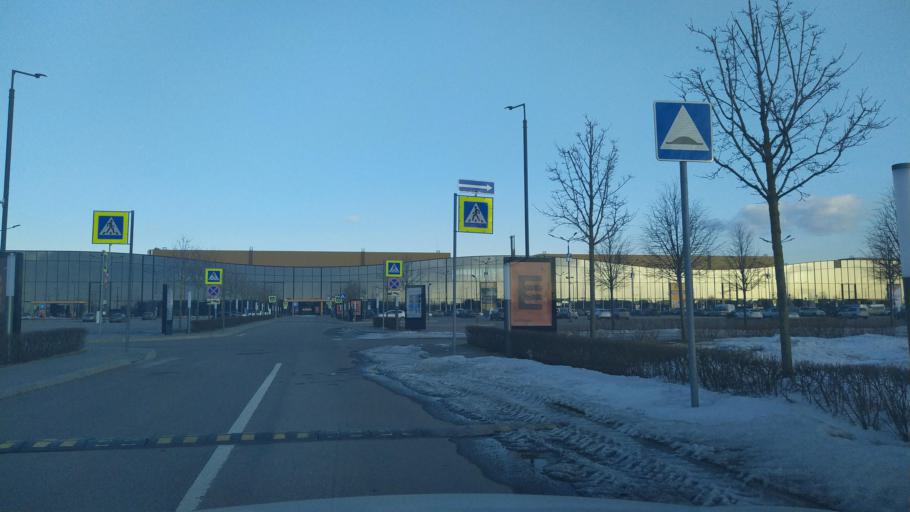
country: RU
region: St.-Petersburg
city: Aleksandrovskaya
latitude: 59.7625
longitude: 30.3509
